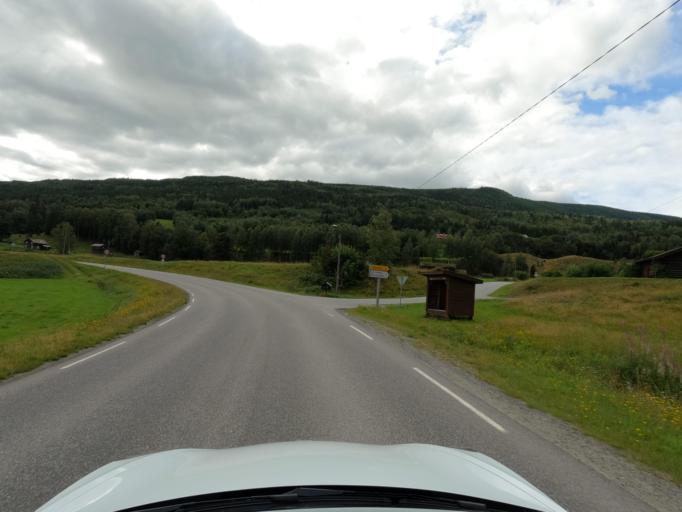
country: NO
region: Telemark
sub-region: Tinn
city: Rjukan
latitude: 59.9859
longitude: 8.7333
